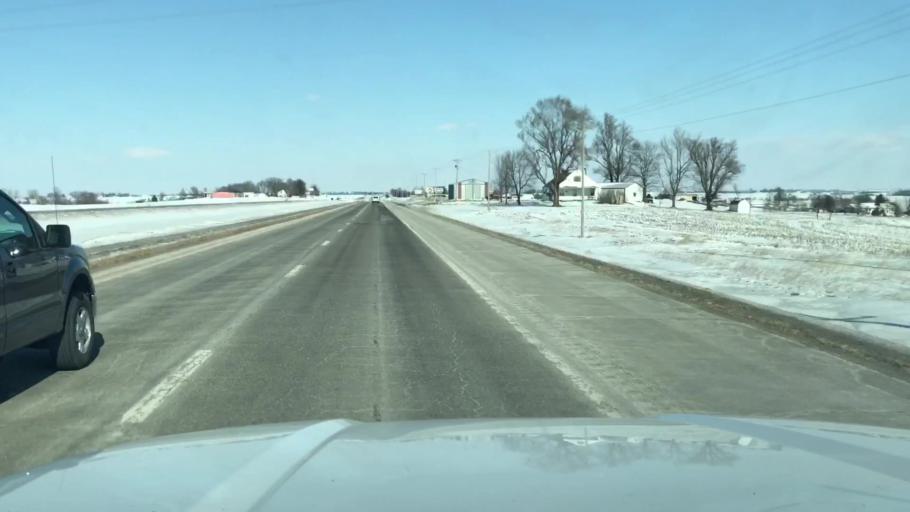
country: US
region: Missouri
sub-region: Nodaway County
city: Maryville
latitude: 40.2819
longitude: -94.8755
